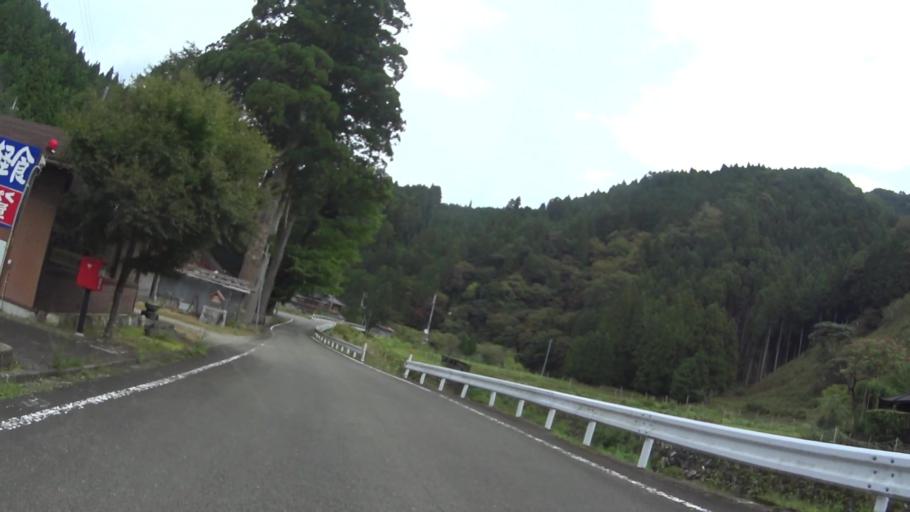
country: JP
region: Fukui
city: Obama
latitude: 35.2812
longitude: 135.6955
